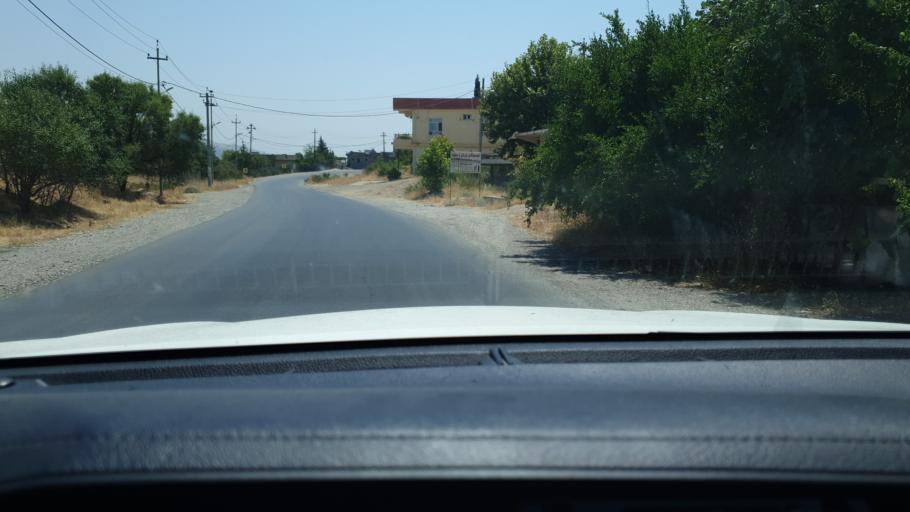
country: IQ
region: Arbil
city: Nahiyat Hiran
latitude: 36.2892
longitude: 44.4834
